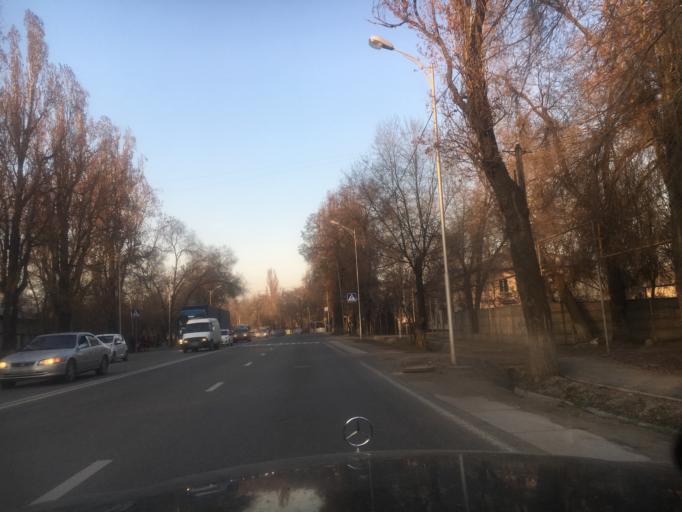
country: KZ
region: Almaty Oblysy
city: Pervomayskiy
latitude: 43.3534
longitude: 76.9751
